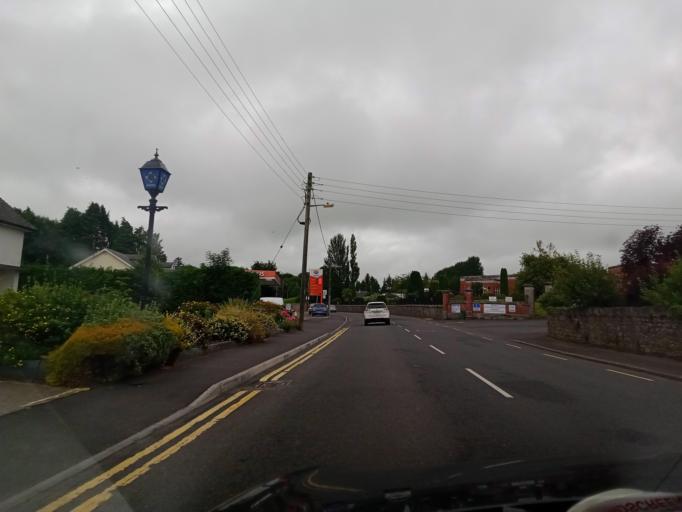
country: IE
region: Leinster
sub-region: Laois
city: Abbeyleix
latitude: 52.9126
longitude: -7.3439
